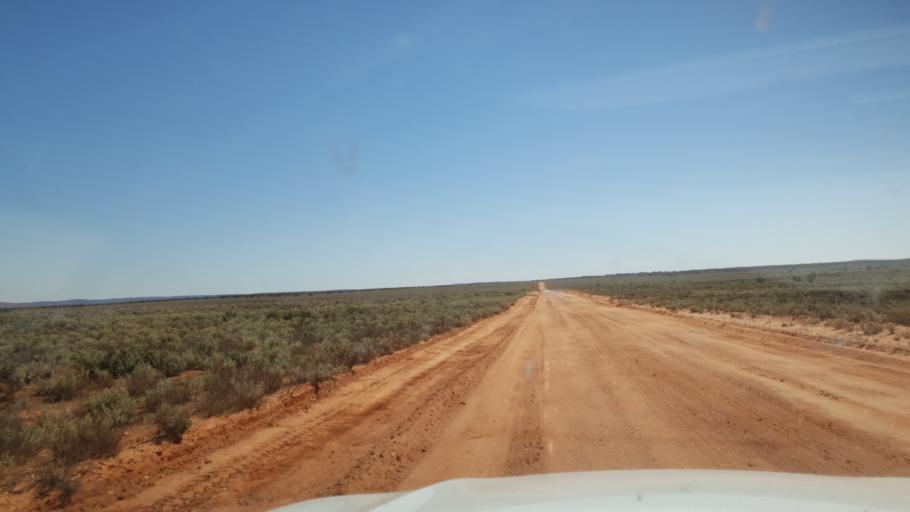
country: AU
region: South Australia
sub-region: Whyalla
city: Whyalla
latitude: -32.6375
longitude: 136.9146
